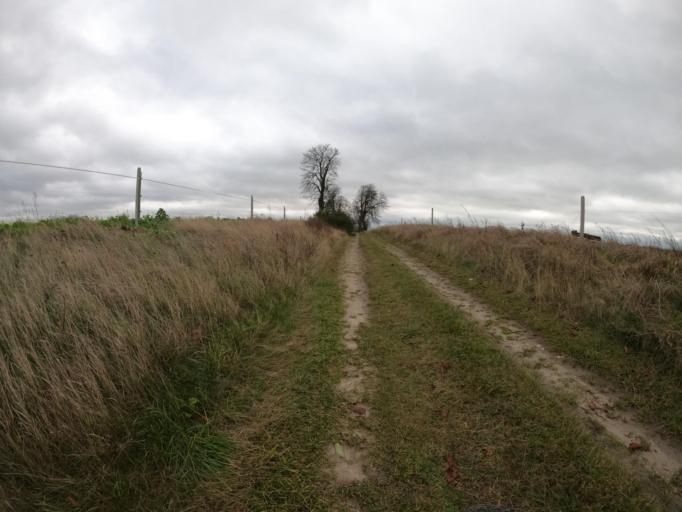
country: PL
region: West Pomeranian Voivodeship
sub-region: Powiat walecki
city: Tuczno
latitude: 53.2488
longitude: 16.2048
